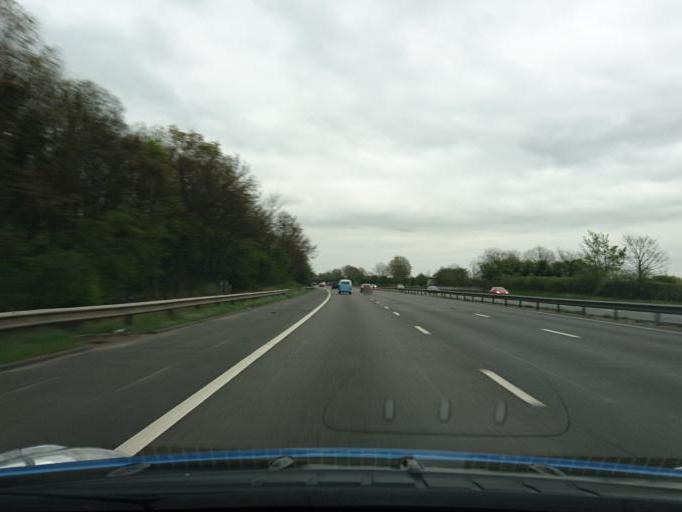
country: GB
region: England
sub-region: Staffordshire
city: Stafford
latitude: 52.7944
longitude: -2.1502
